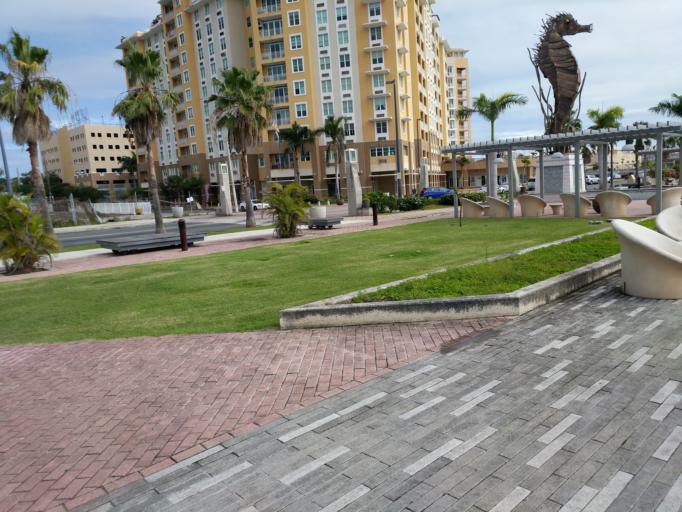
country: PR
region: San Juan
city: San Juan
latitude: 18.4636
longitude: -66.1083
